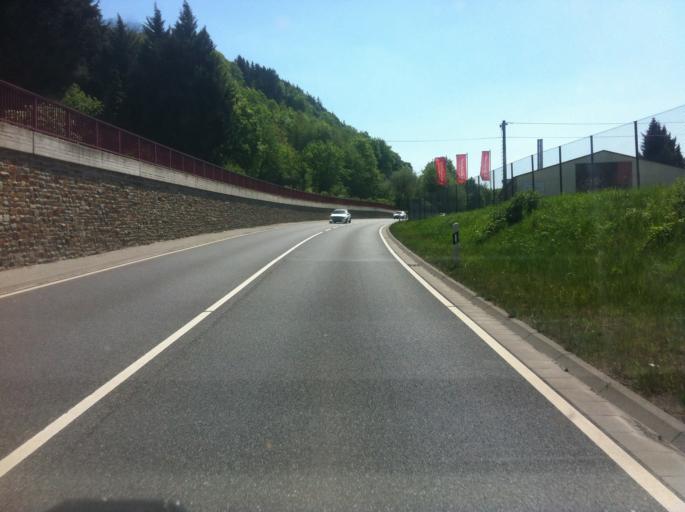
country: DE
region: Rheinland-Pfalz
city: Unkel
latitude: 50.6045
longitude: 7.2215
